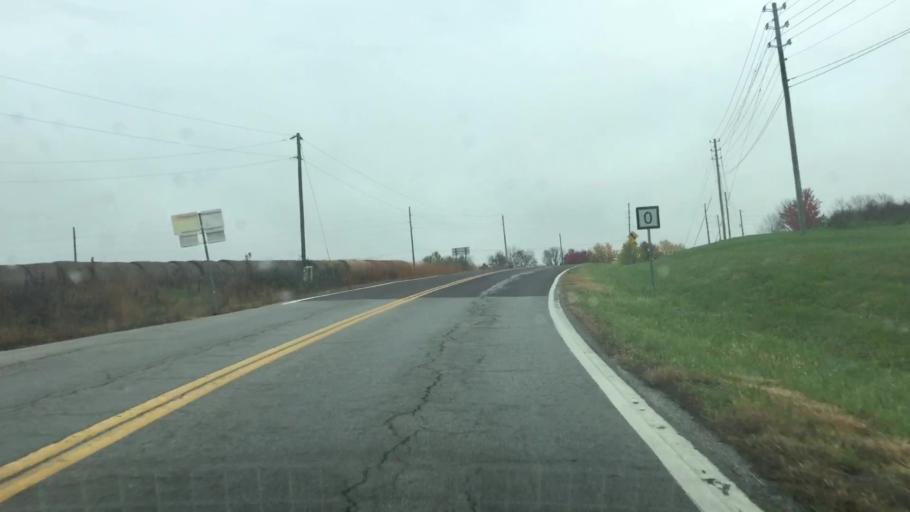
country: US
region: Missouri
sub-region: Callaway County
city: Fulton
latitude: 38.8404
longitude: -91.9236
